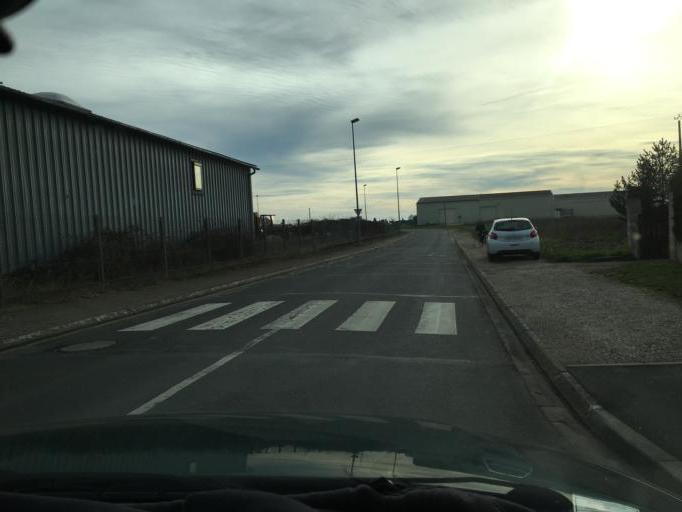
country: FR
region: Centre
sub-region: Departement du Loiret
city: Baule
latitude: 47.8129
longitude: 1.6641
